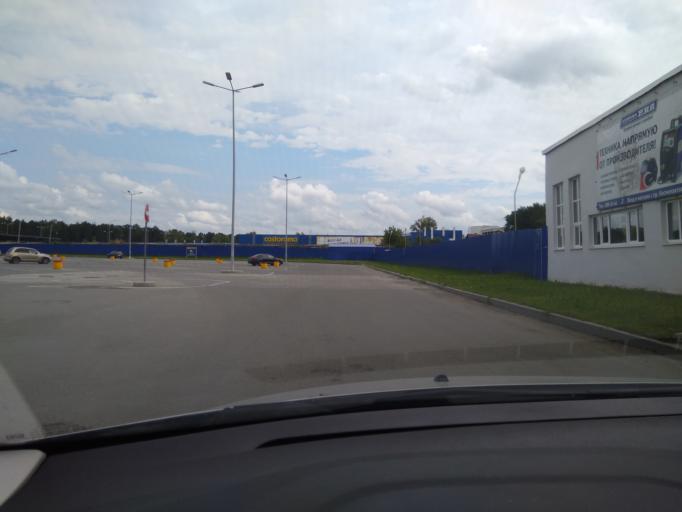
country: RU
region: Sverdlovsk
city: Yekaterinburg
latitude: 56.9114
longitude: 60.6128
